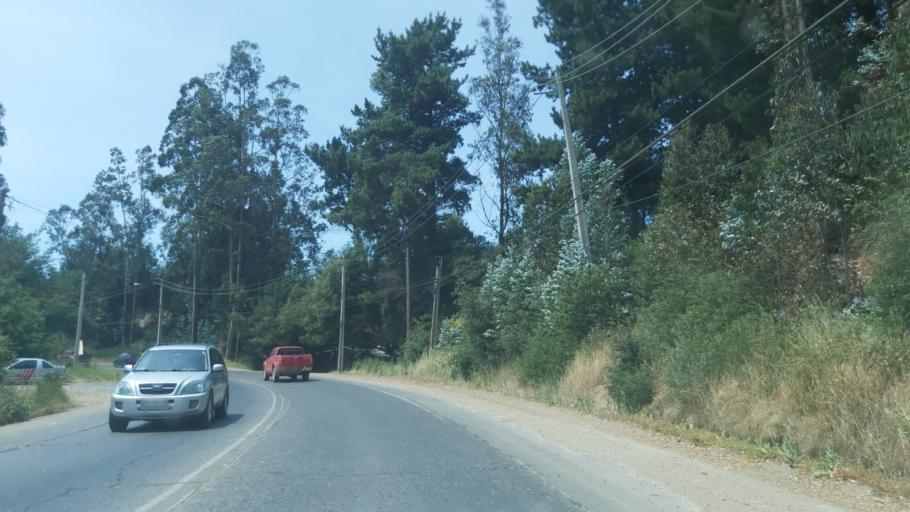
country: CL
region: Maule
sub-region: Provincia de Talca
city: Constitucion
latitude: -35.3515
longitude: -72.4088
